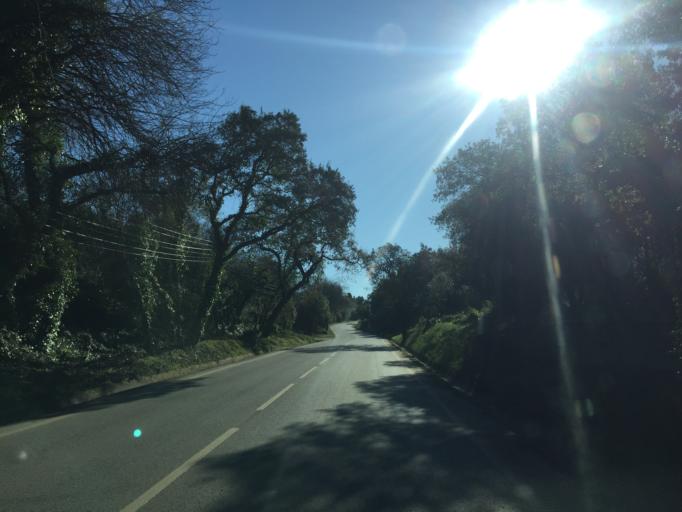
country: PT
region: Lisbon
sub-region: Sintra
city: Almargem
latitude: 38.8095
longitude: -9.2903
